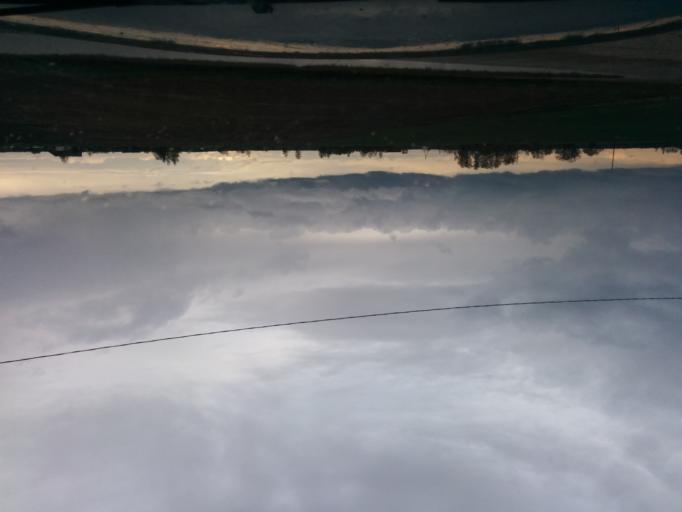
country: LT
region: Siauliu apskritis
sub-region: Joniskis
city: Joniskis
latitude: 56.3728
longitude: 23.5462
